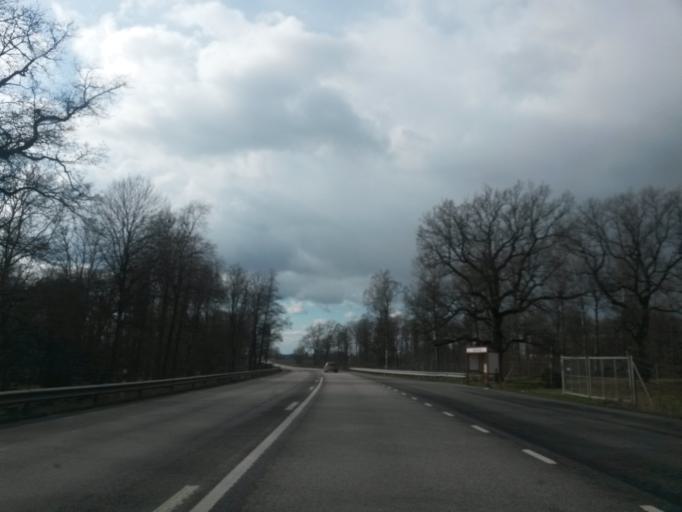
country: SE
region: Vaestra Goetaland
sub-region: Skara Kommun
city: Axvall
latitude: 58.3820
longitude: 13.6794
